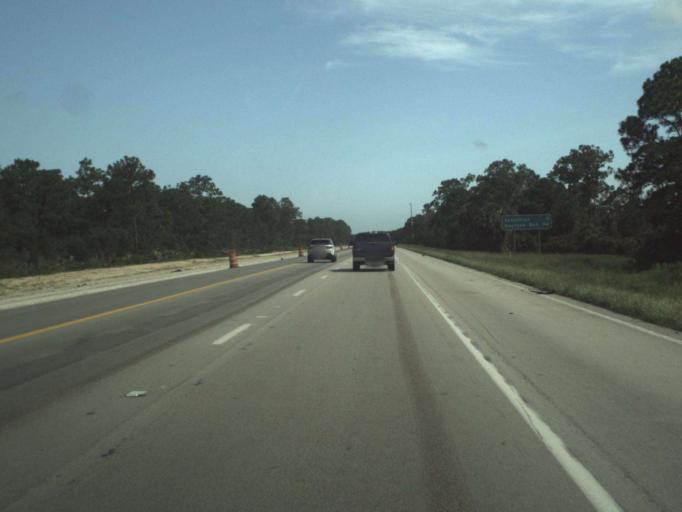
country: US
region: Florida
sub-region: Indian River County
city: West Vero Corridor
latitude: 27.6540
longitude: -80.5231
